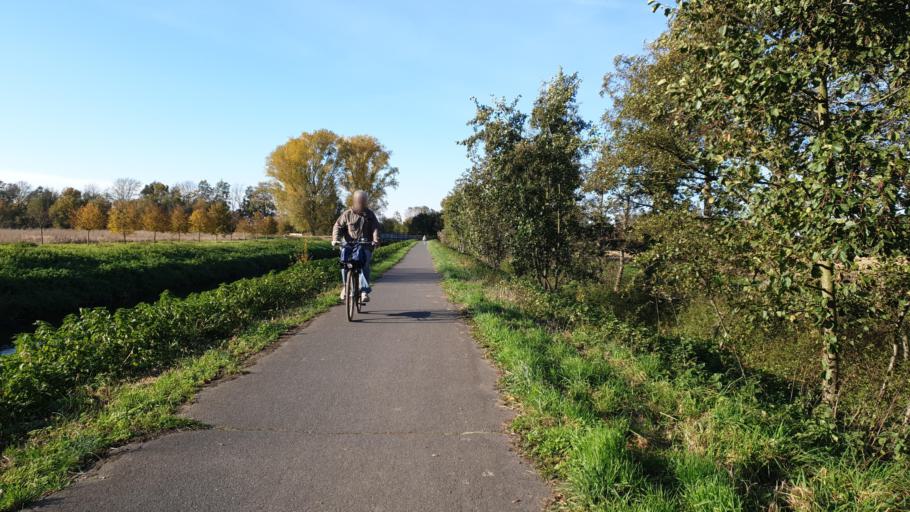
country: DE
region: North Rhine-Westphalia
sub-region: Regierungsbezirk Koln
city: Kerpen
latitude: 50.9239
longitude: 6.6851
